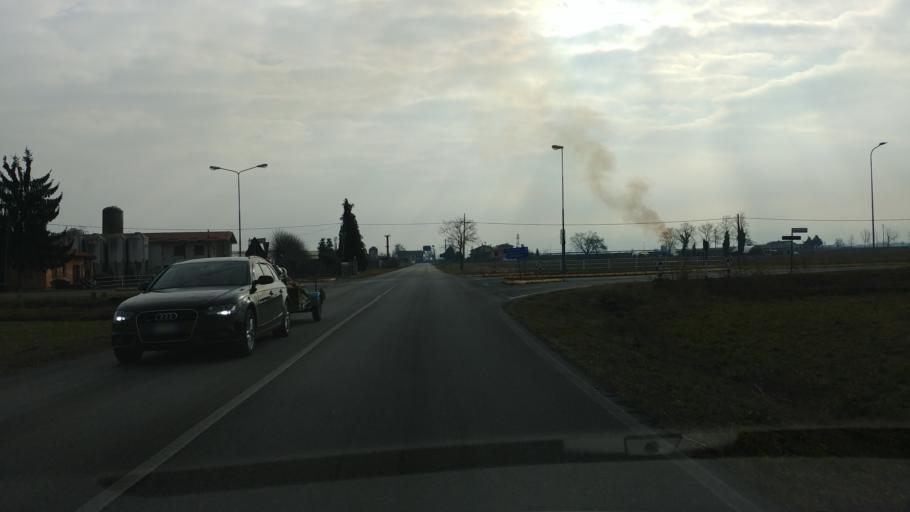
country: IT
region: Piedmont
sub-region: Provincia di Cuneo
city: Castelletto Stura
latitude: 44.4498
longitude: 7.6470
